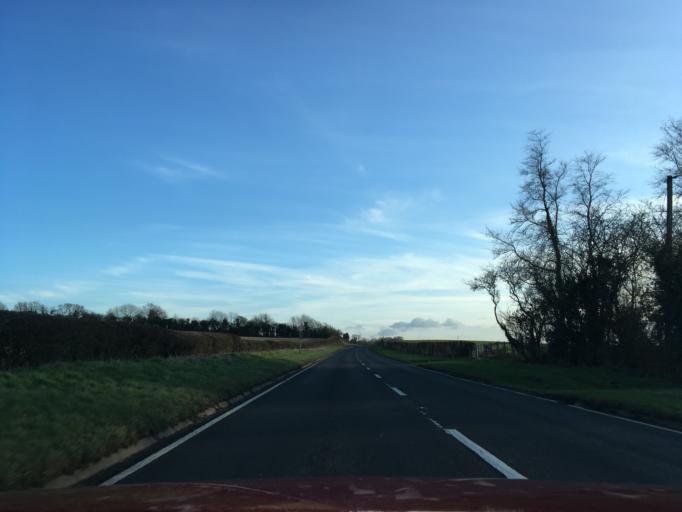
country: GB
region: England
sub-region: Warwickshire
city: Stratford-upon-Avon
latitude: 52.2385
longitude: -1.7444
